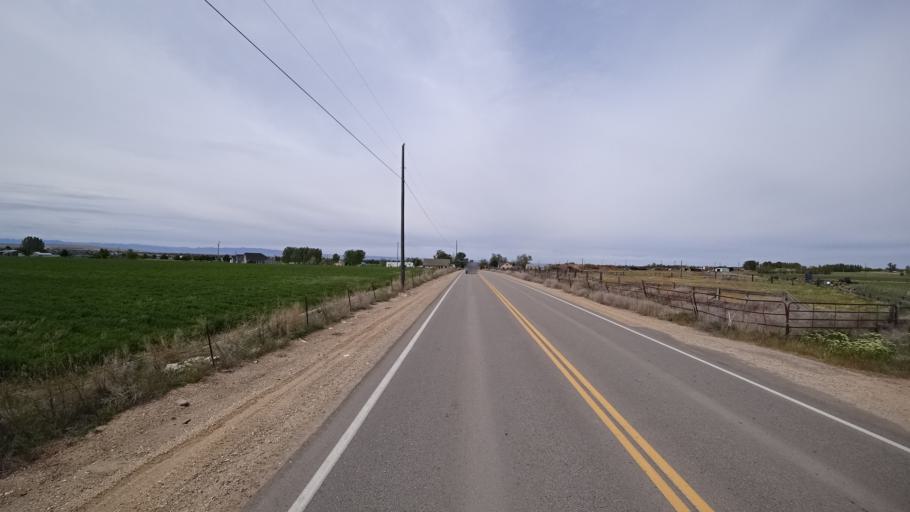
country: US
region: Idaho
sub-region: Ada County
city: Kuna
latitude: 43.5318
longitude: -116.3702
